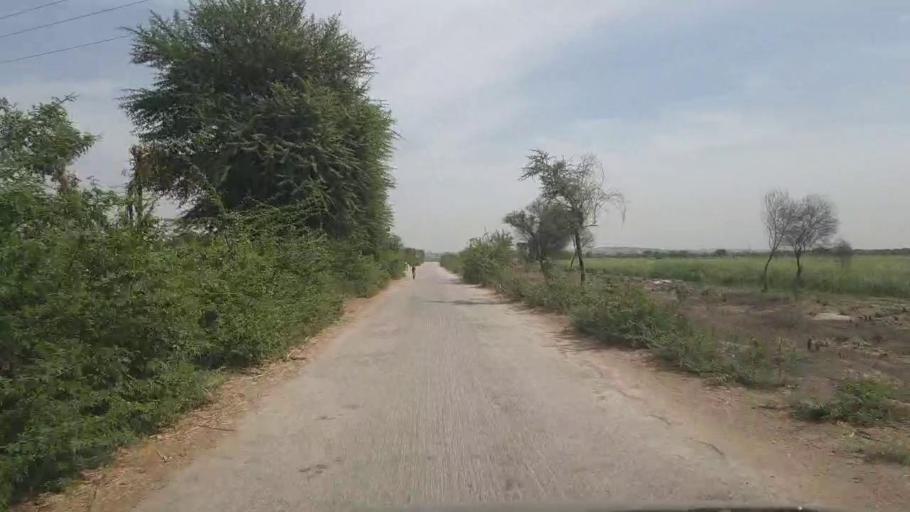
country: PK
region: Sindh
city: Kunri
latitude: 25.2235
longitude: 69.6922
